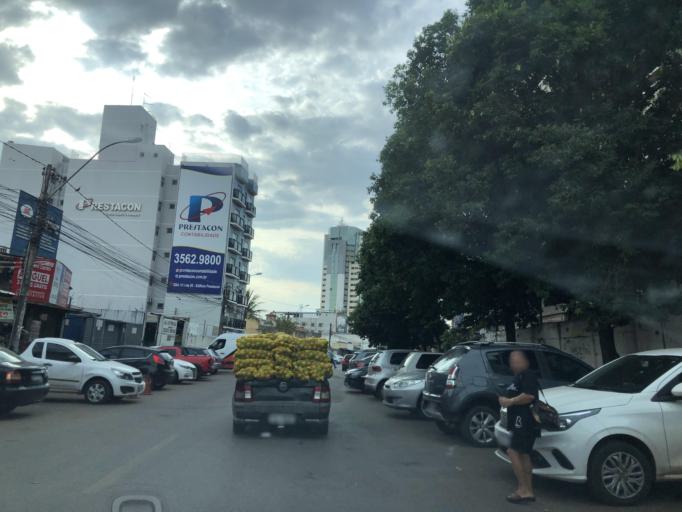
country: BR
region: Federal District
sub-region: Brasilia
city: Brasilia
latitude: -15.8352
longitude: -48.0520
